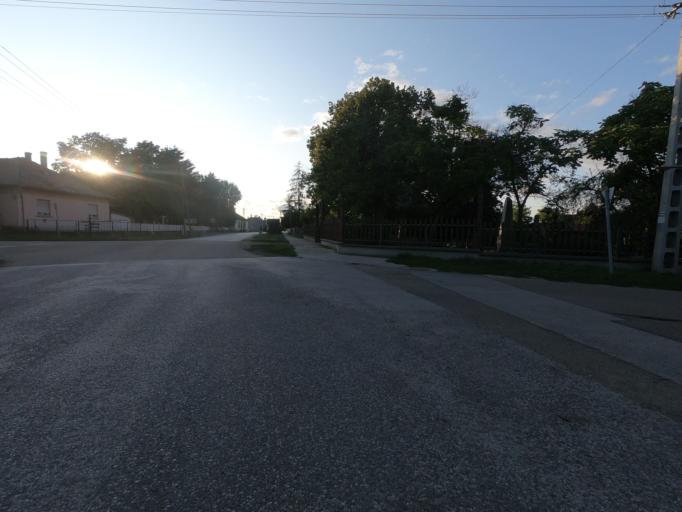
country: HU
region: Heves
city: Szihalom
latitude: 47.7196
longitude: 20.4795
